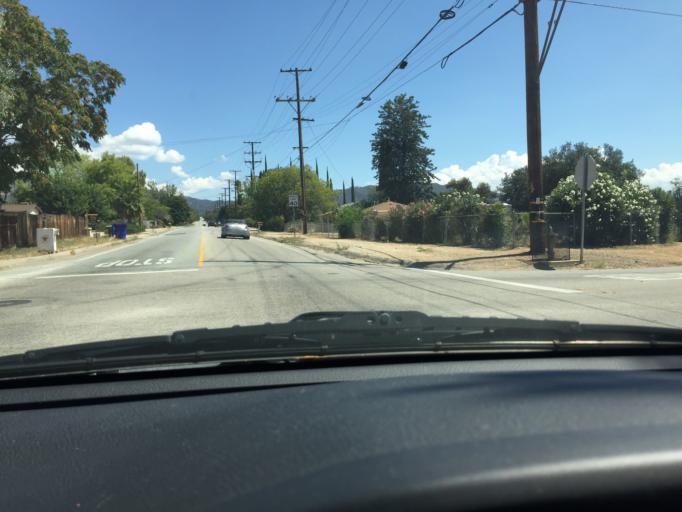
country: US
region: California
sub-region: San Bernardino County
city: Yucaipa
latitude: 34.0158
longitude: -117.0477
